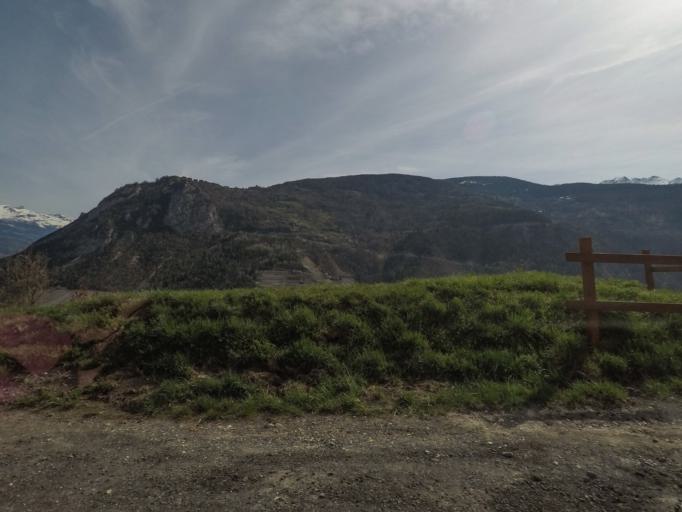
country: CH
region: Valais
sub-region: Herens District
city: Vex
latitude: 46.2176
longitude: 7.4034
